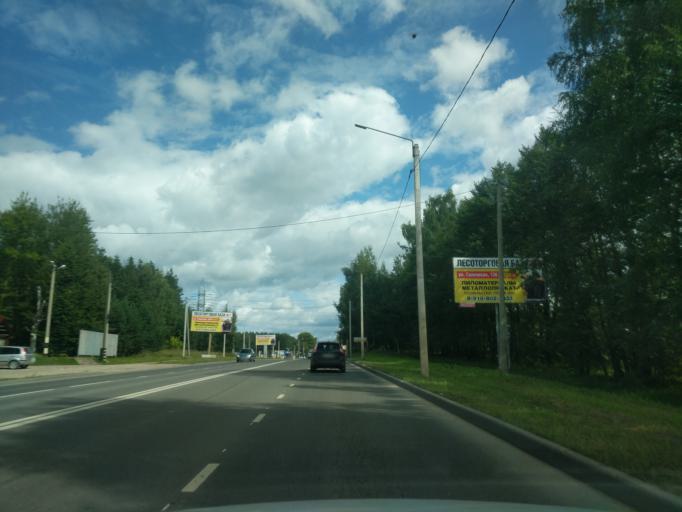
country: RU
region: Kostroma
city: Oktyabr'skiy
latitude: 57.7808
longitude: 40.9859
